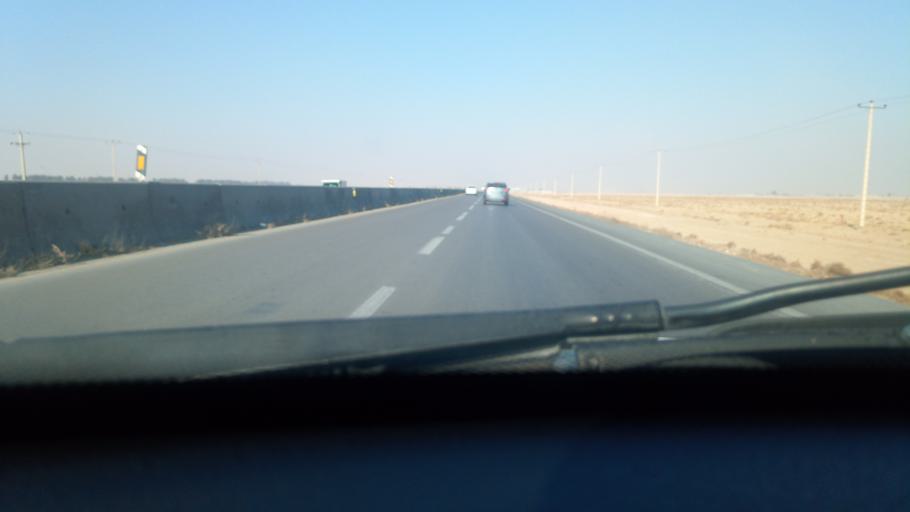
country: IR
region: Razavi Khorasan
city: Chenaran
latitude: 36.7691
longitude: 58.9173
